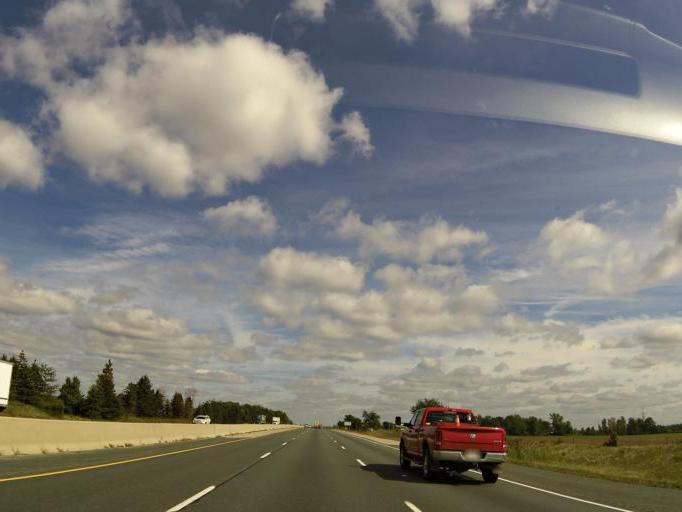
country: CA
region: Ontario
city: Dorchester
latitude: 42.9566
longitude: -81.0719
